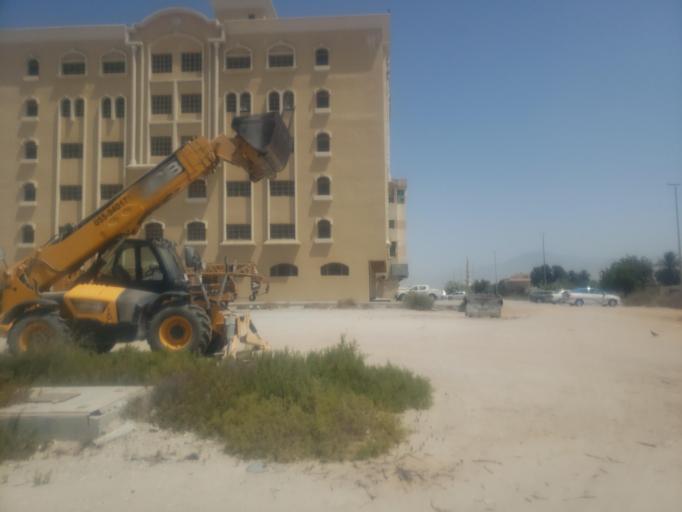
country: AE
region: Ra's al Khaymah
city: Ras al-Khaimah
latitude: 25.8079
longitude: 55.9592
